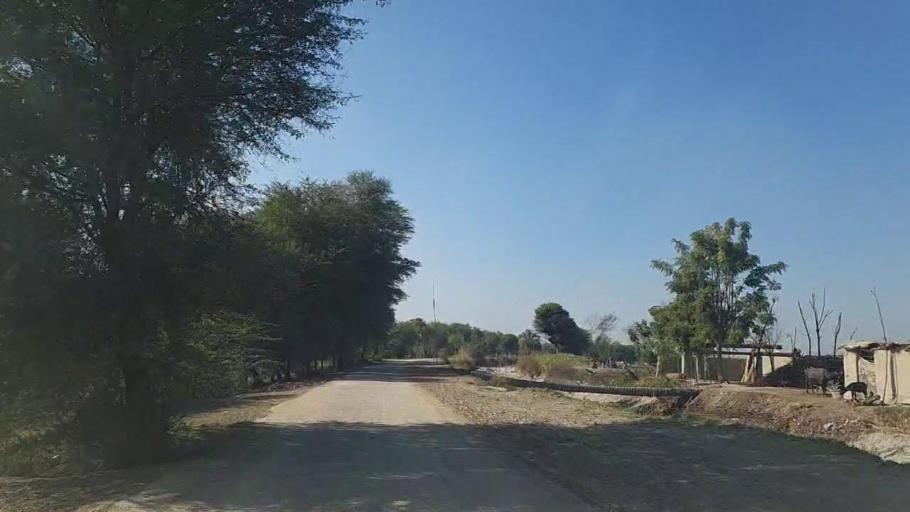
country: PK
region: Sindh
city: Shahpur Chakar
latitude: 26.2143
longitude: 68.6089
